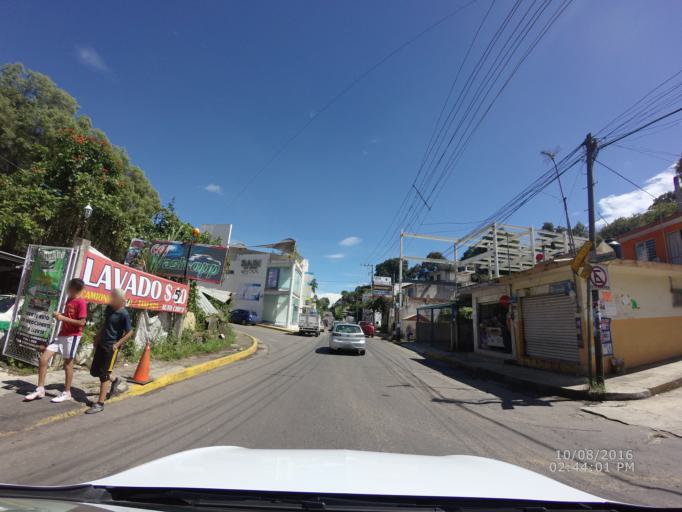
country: MX
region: Veracruz
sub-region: Xalapa
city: Lomas Verdes
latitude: 19.5084
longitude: -96.9017
